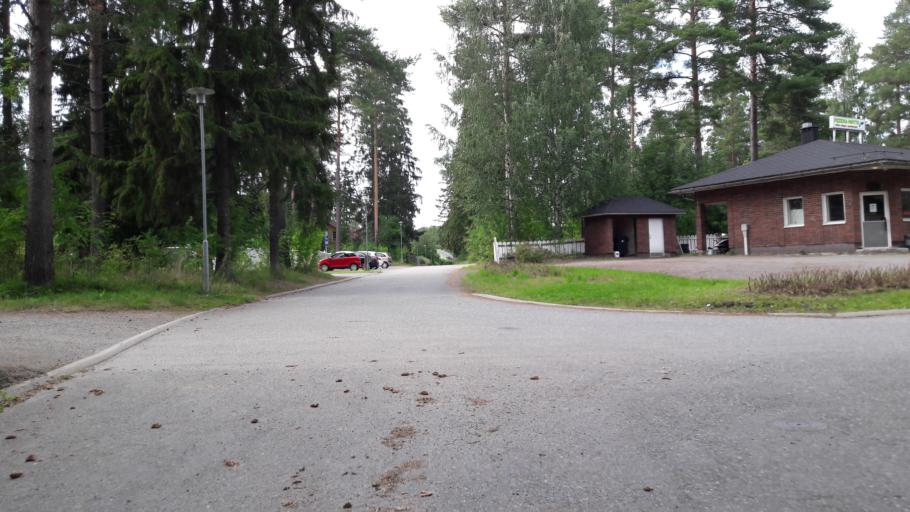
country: FI
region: North Karelia
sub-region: Joensuu
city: Joensuu
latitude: 62.5806
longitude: 29.7665
